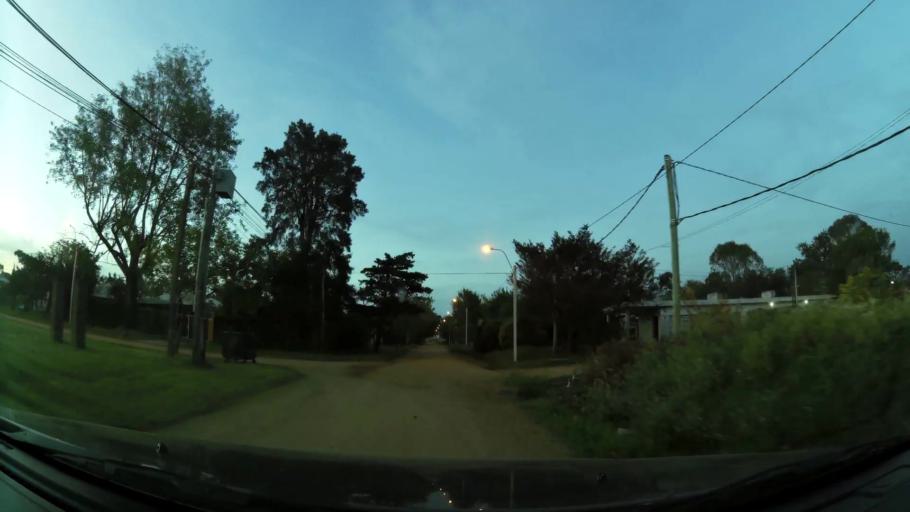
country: UY
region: Canelones
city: Atlantida
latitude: -34.7739
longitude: -55.7490
